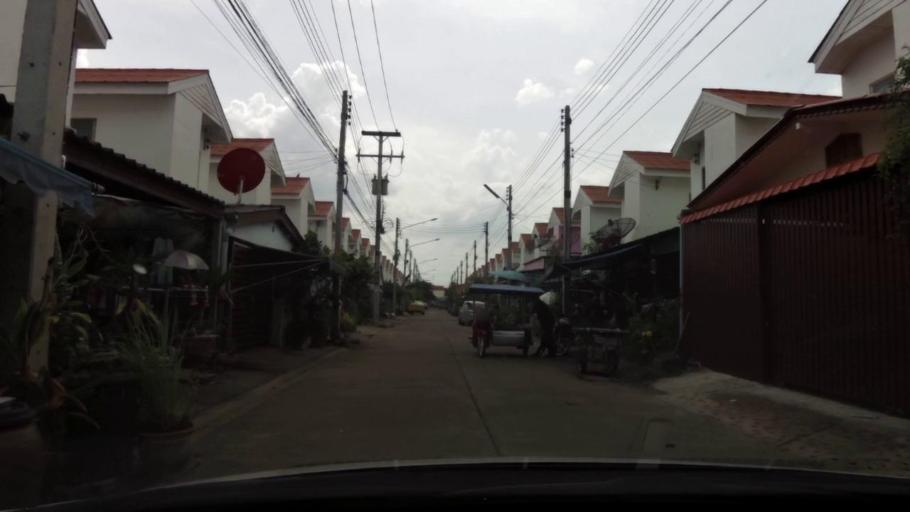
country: TH
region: Ratchaburi
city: Ratchaburi
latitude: 13.5389
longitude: 99.7938
